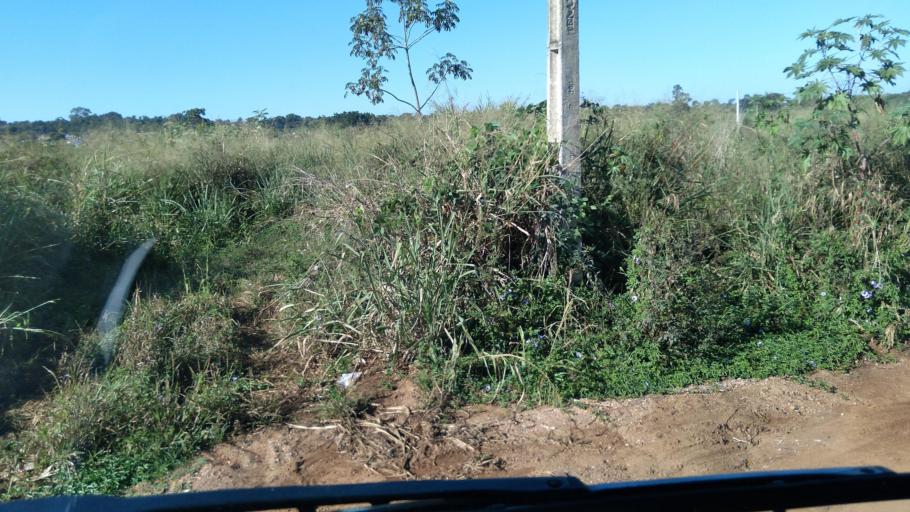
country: BR
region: Goias
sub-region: Mineiros
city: Mineiros
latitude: -17.5785
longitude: -52.5682
